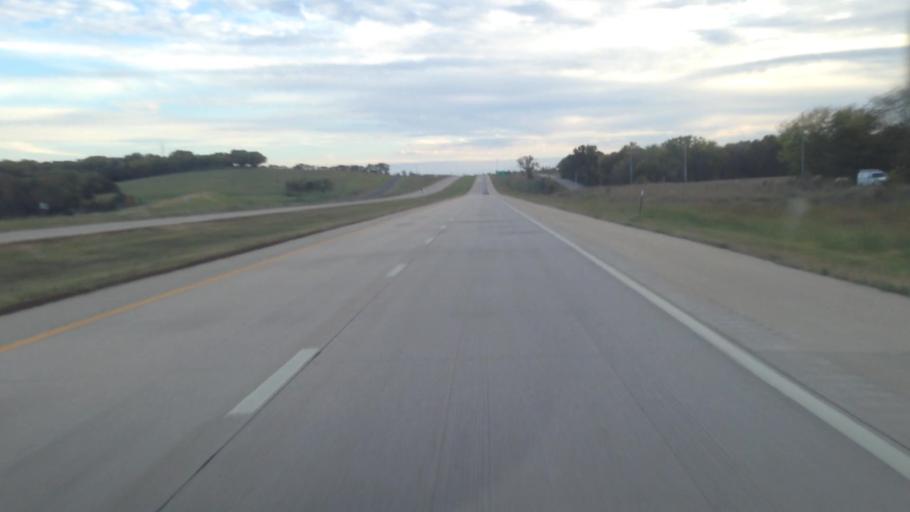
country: US
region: Kansas
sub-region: Douglas County
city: Baldwin City
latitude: 38.8020
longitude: -95.2692
